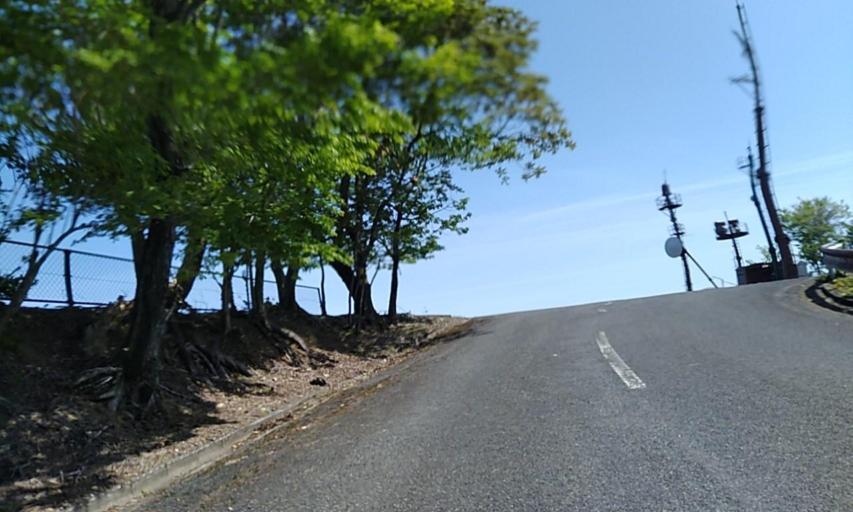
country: JP
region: Fukui
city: Obama
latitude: 35.5488
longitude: 135.7444
